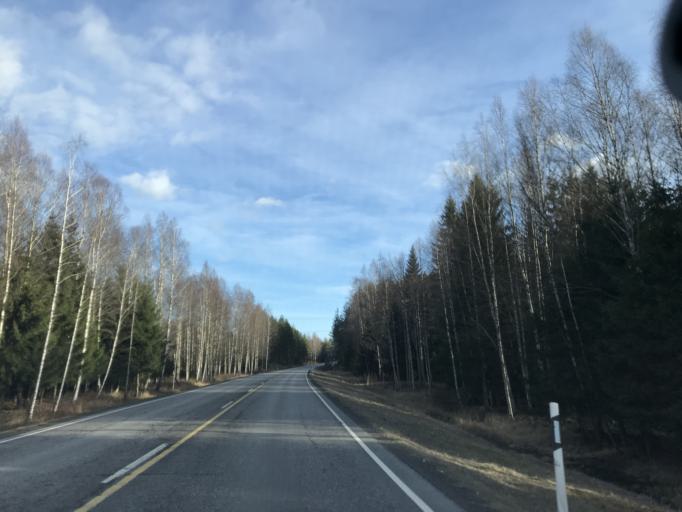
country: FI
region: Varsinais-Suomi
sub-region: Salo
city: Pernioe
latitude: 60.0768
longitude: 23.2596
